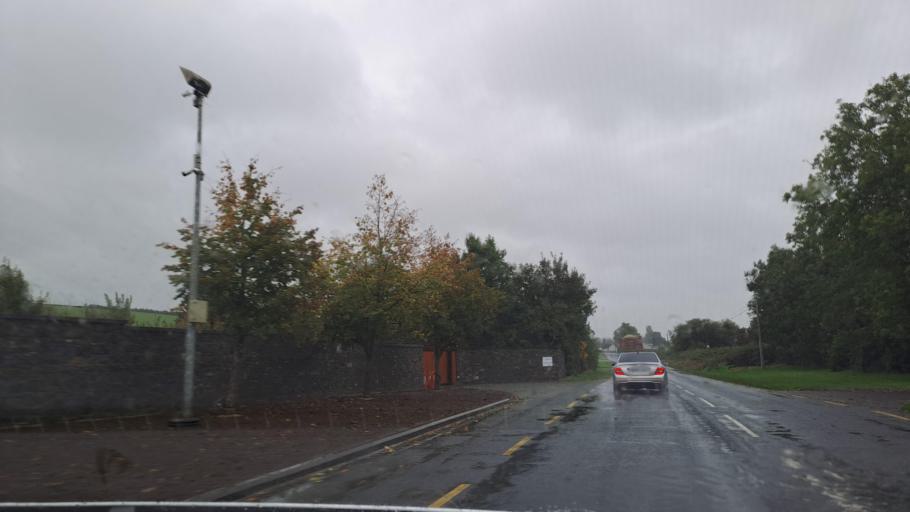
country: IE
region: Ulster
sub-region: County Monaghan
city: Carrickmacross
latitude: 53.9736
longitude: -6.6712
